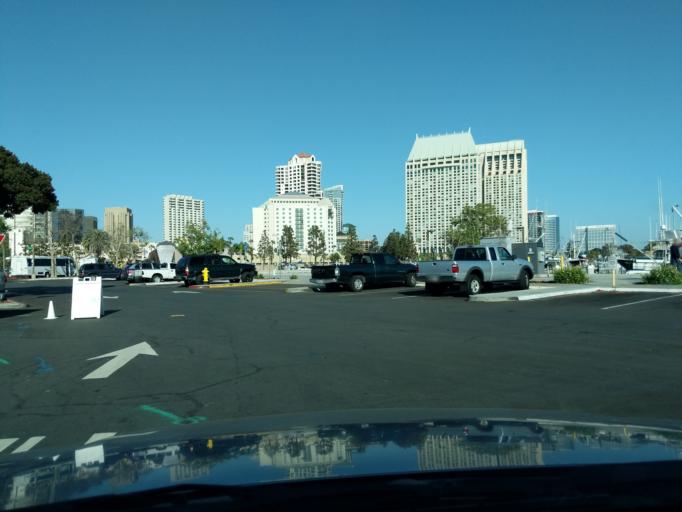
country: US
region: California
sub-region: San Diego County
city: San Diego
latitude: 32.7121
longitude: -117.1747
